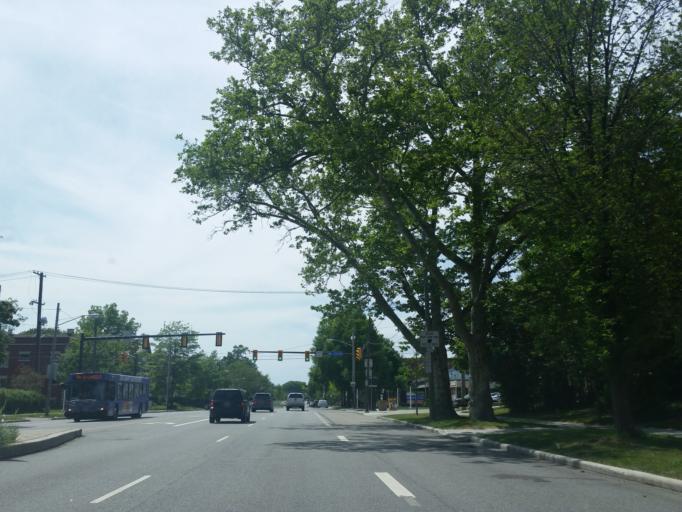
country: US
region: Ohio
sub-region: Cuyahoga County
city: Lakewood
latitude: 41.4860
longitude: -81.7601
